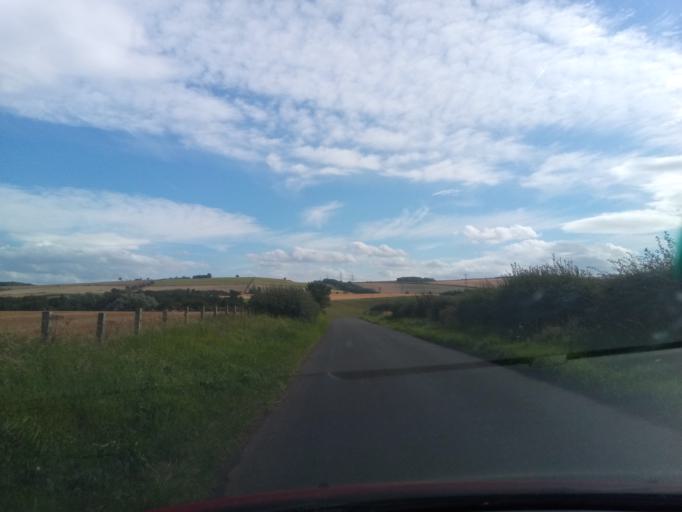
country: GB
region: Scotland
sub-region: The Scottish Borders
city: Coldstream
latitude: 55.6369
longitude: -2.1901
